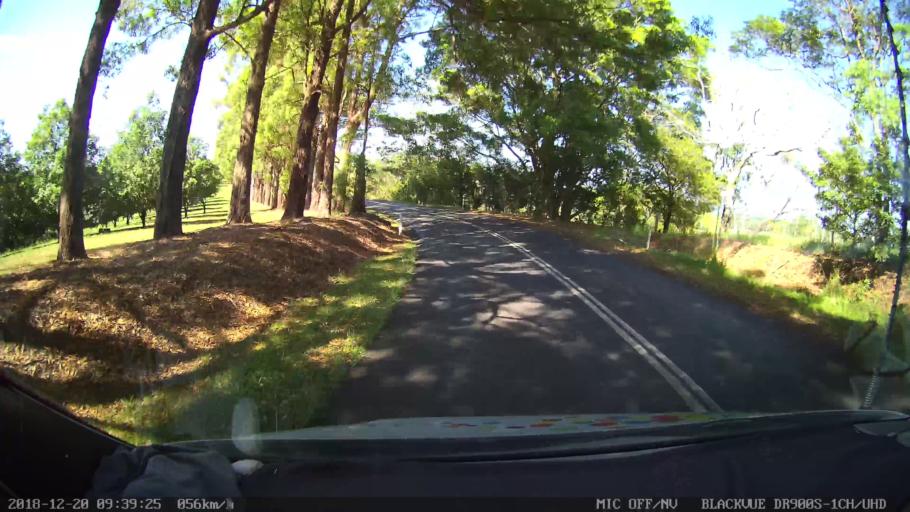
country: AU
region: New South Wales
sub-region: Lismore Municipality
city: Goonellabah
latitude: -28.6952
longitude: 153.3085
